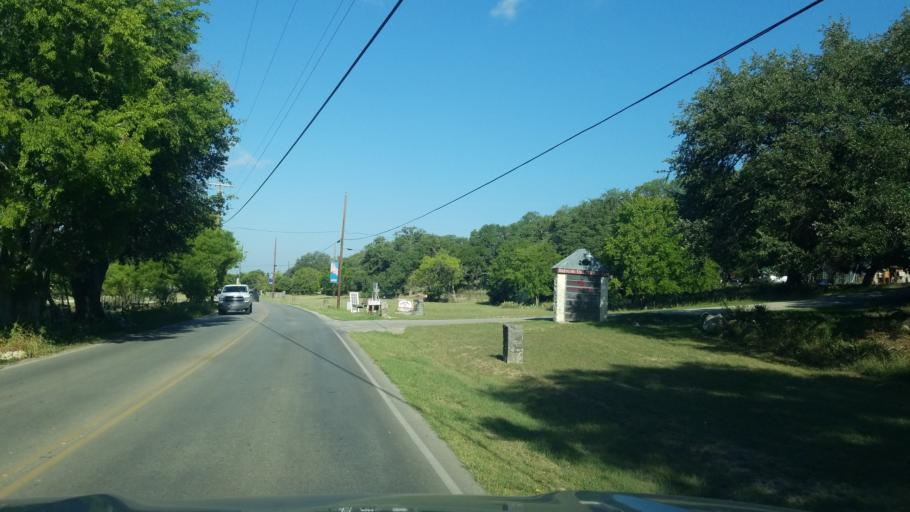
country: US
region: Texas
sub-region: Comal County
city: Bulverde
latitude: 29.7428
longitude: -98.4465
